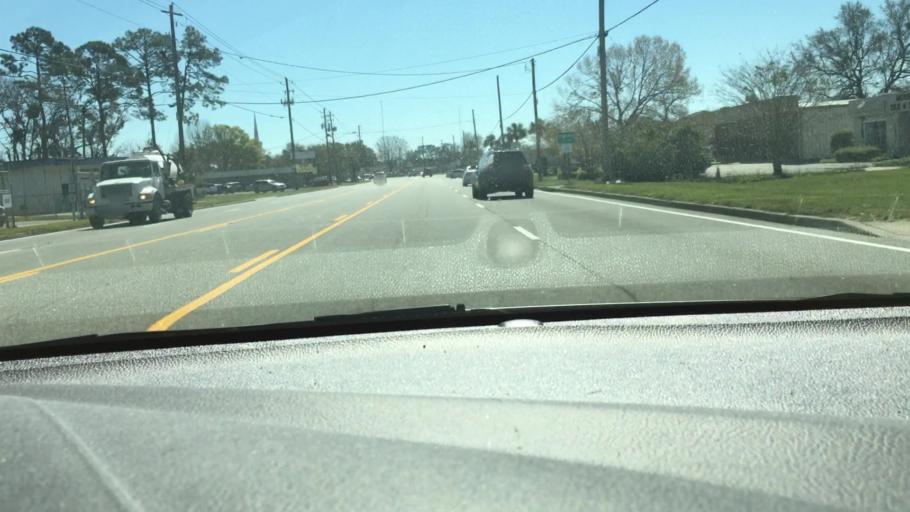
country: US
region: Georgia
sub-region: Glynn County
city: Dock Junction
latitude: 31.1985
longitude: -81.4912
